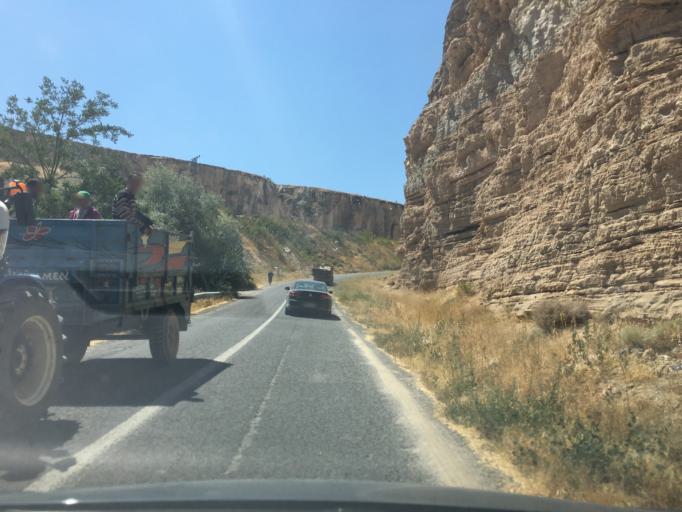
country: TR
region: Nevsehir
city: Urgub
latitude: 38.4654
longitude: 34.9362
